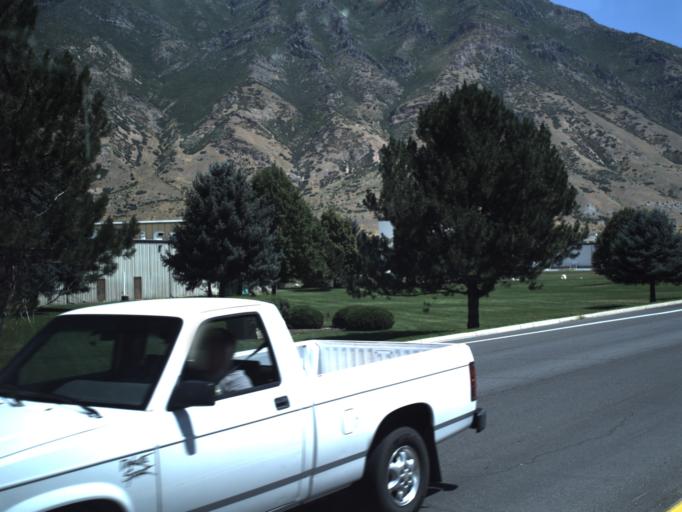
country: US
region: Utah
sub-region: Utah County
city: Springville
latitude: 40.1876
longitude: -111.6309
